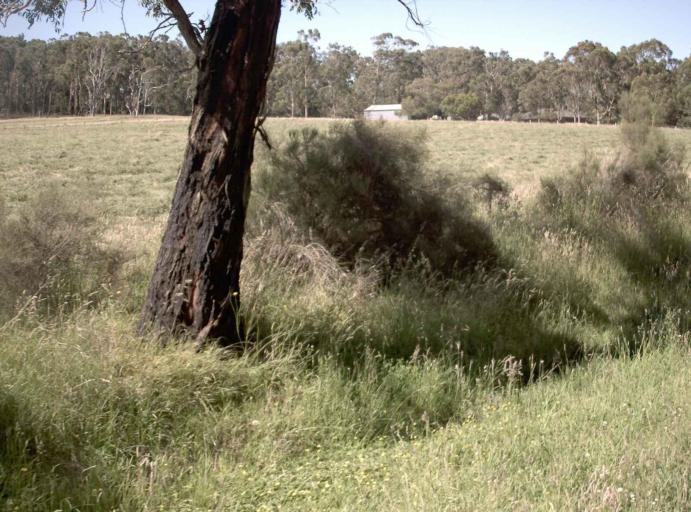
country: AU
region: Victoria
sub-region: Latrobe
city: Morwell
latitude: -38.6472
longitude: 146.4732
